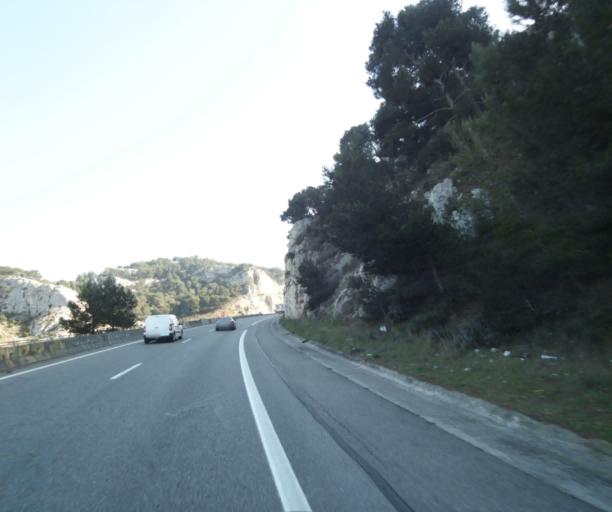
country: FR
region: Provence-Alpes-Cote d'Azur
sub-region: Departement des Bouches-du-Rhone
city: Les Pennes-Mirabeau
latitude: 43.3979
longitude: 5.2974
